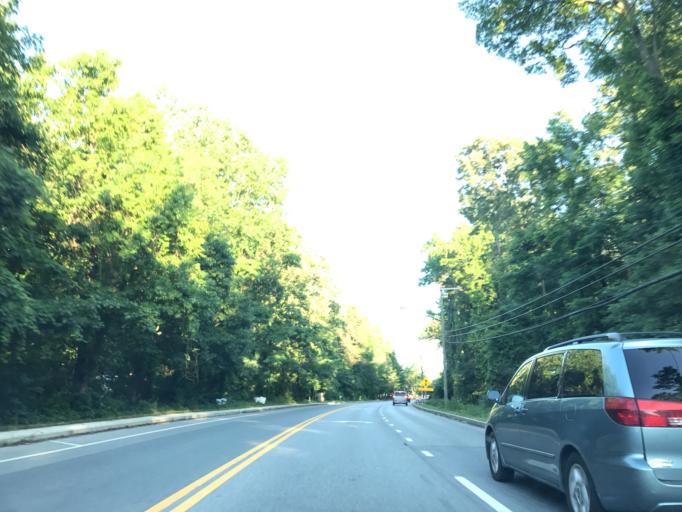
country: US
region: Maryland
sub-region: Anne Arundel County
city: Crofton
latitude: 39.0138
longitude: -76.6846
